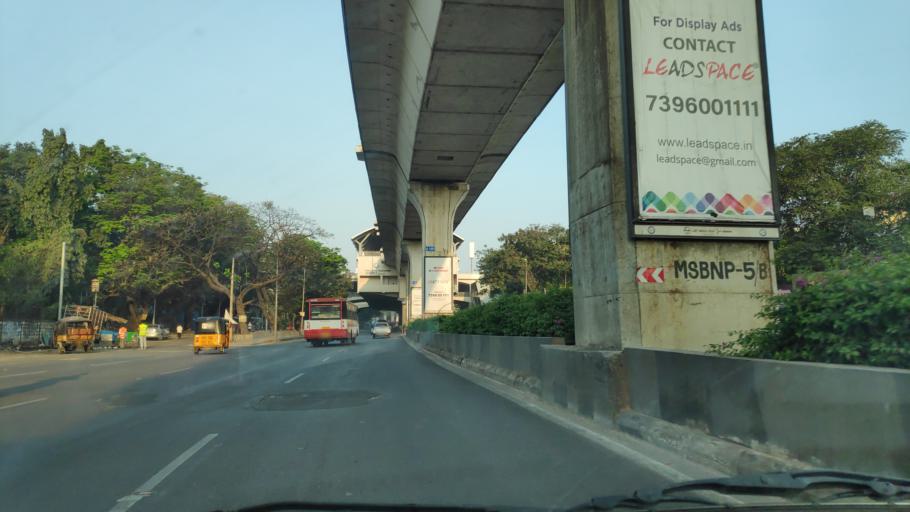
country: IN
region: Telangana
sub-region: Rangareddi
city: Gaddi Annaram
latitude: 17.3702
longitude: 78.5136
